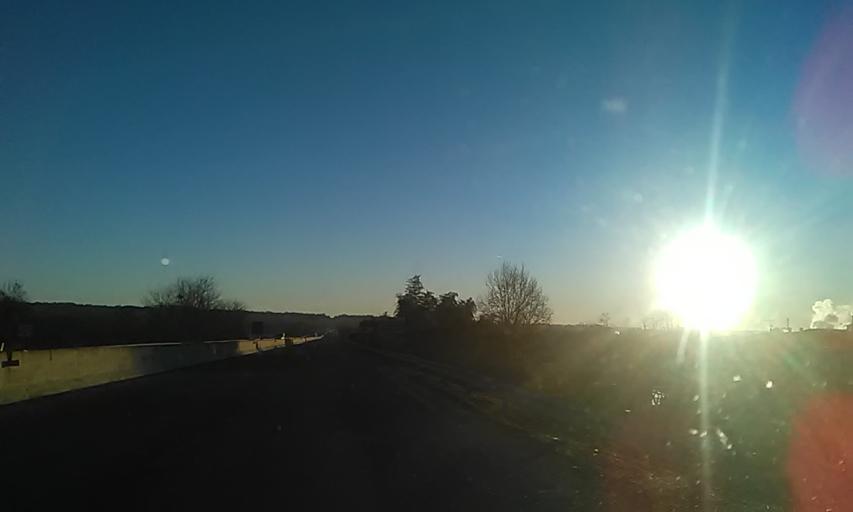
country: IT
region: Piedmont
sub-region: Provincia di Biella
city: Cerreto Castello
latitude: 45.5531
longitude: 8.1742
